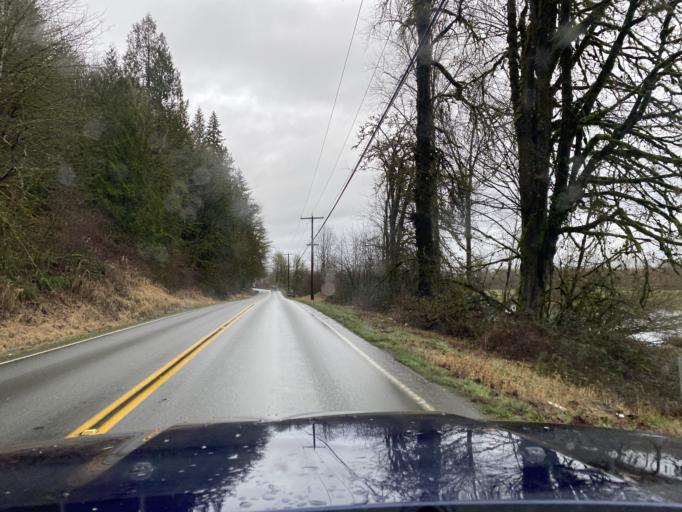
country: US
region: Washington
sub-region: King County
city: Duvall
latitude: 47.7159
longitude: -122.0080
